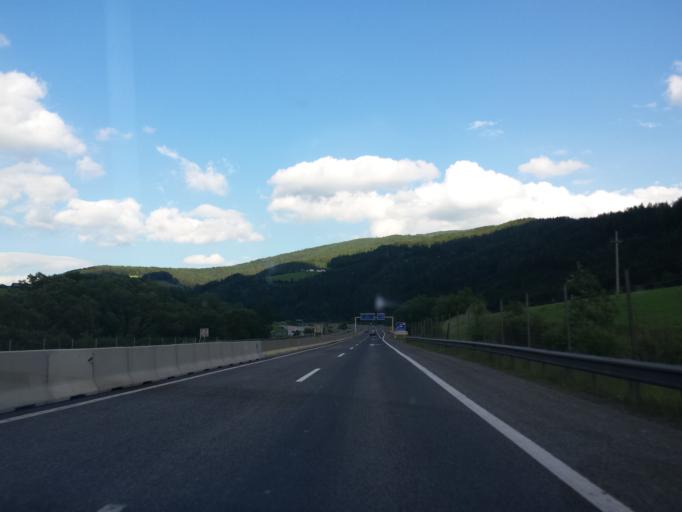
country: AT
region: Styria
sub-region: Politischer Bezirk Bruck-Muerzzuschlag
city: Muerzzuschlag
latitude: 47.6029
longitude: 15.7132
